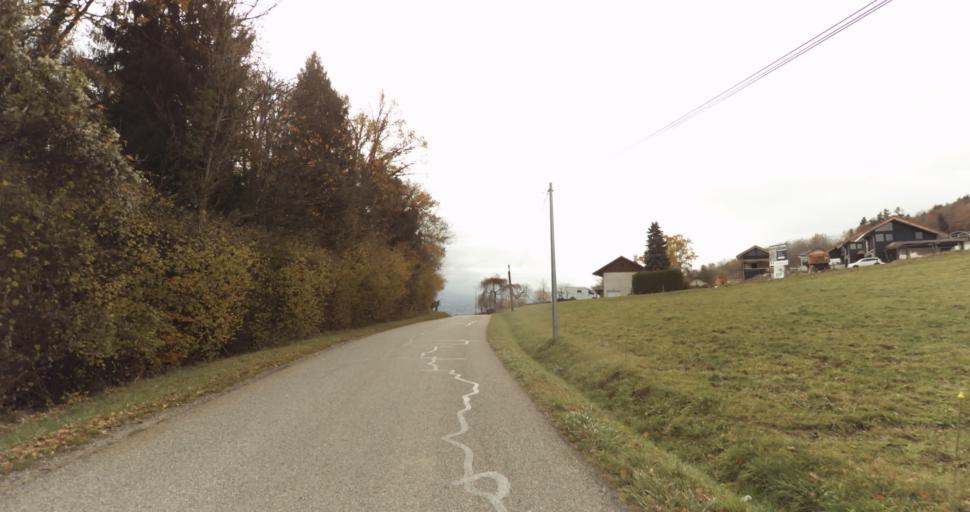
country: FR
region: Rhone-Alpes
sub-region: Departement de la Haute-Savoie
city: Epagny
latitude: 45.9595
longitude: 6.1039
